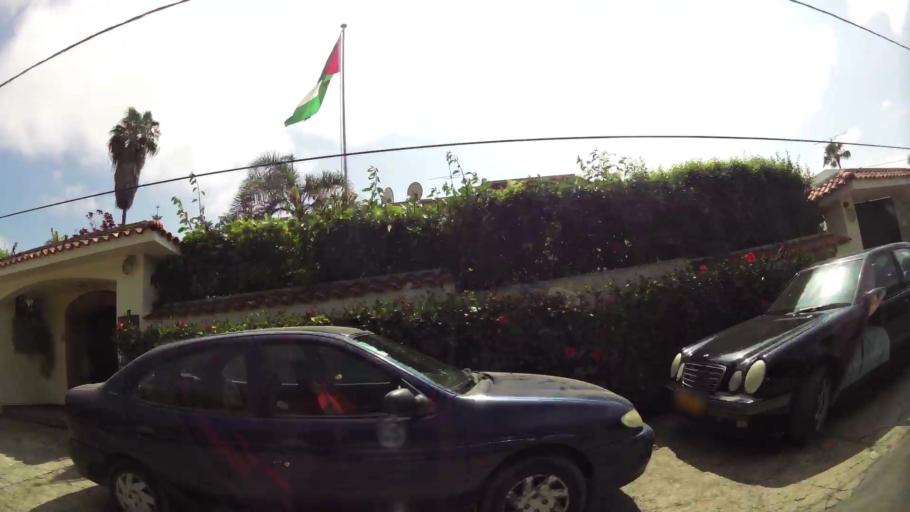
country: MA
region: Rabat-Sale-Zemmour-Zaer
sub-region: Rabat
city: Rabat
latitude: 33.9790
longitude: -6.8394
